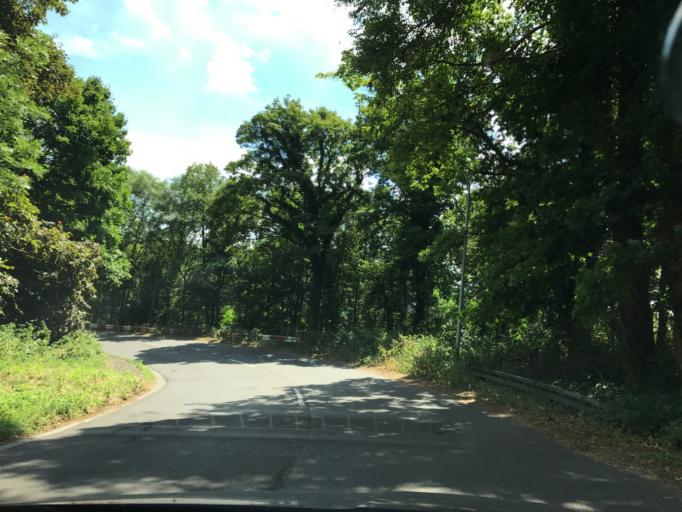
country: DE
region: North Rhine-Westphalia
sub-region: Regierungsbezirk Dusseldorf
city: Heiligenhaus
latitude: 51.3830
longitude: 6.9776
